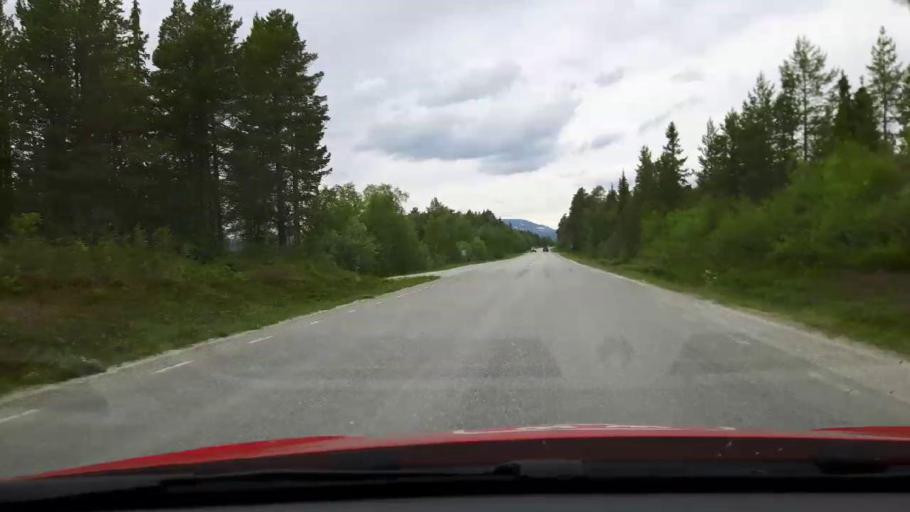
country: NO
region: Hedmark
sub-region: Engerdal
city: Engerdal
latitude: 62.5240
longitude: 12.5866
